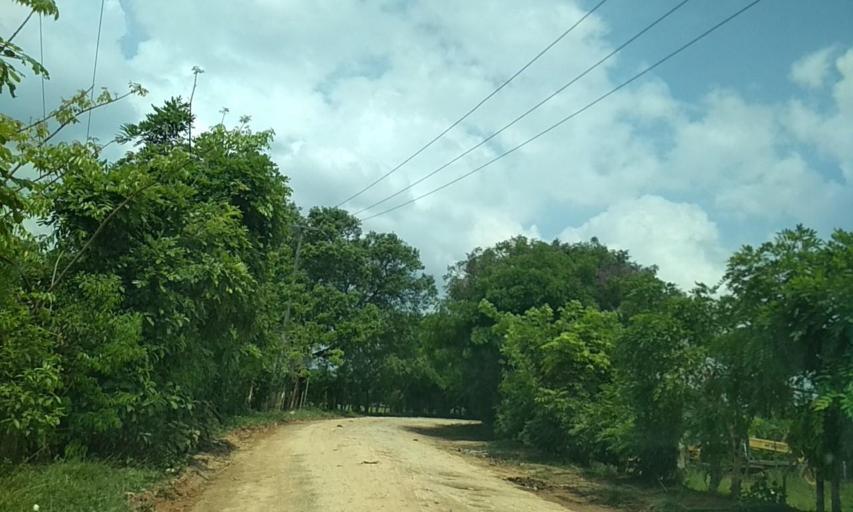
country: MX
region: Veracruz
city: Las Choapas
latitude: 17.8889
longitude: -94.1132
